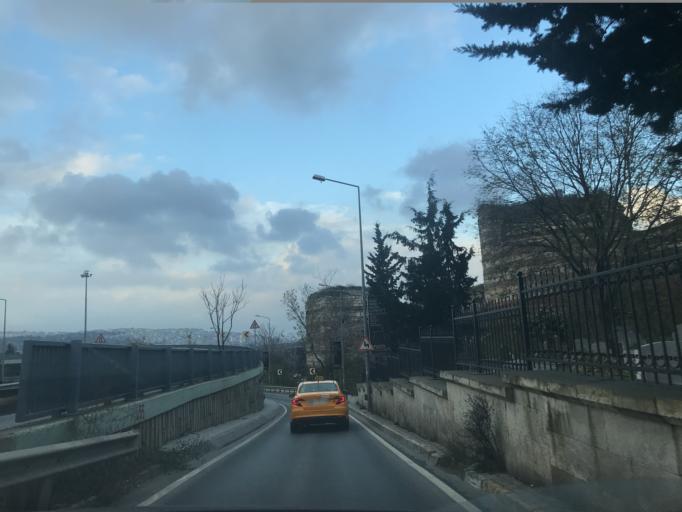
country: TR
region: Istanbul
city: Istanbul
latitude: 41.0364
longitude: 28.9388
